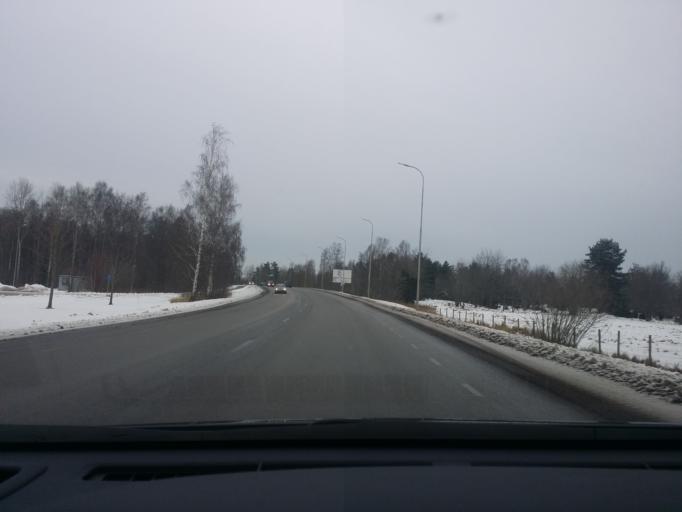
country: SE
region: Vaestra Goetaland
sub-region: Mariestads Kommun
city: Mariestad
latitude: 58.6881
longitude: 13.8191
